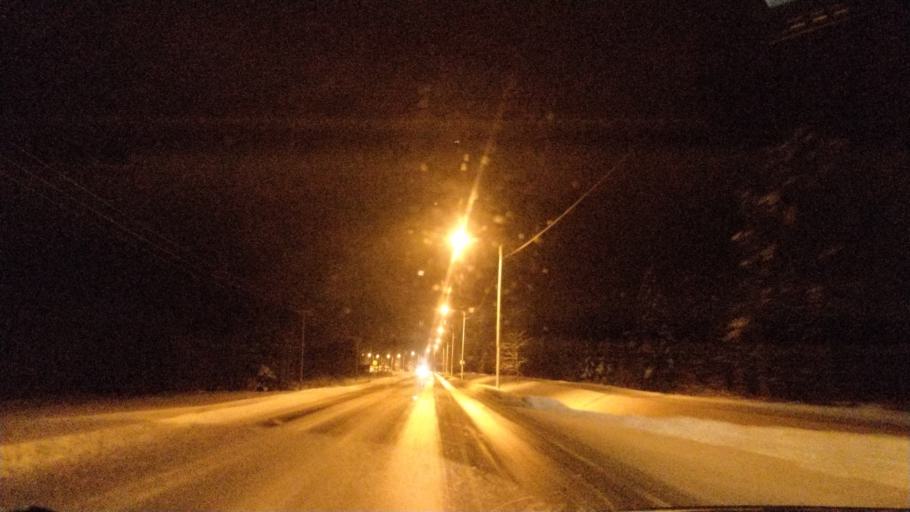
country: FI
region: Lapland
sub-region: Rovaniemi
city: Rovaniemi
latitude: 66.3044
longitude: 25.3566
